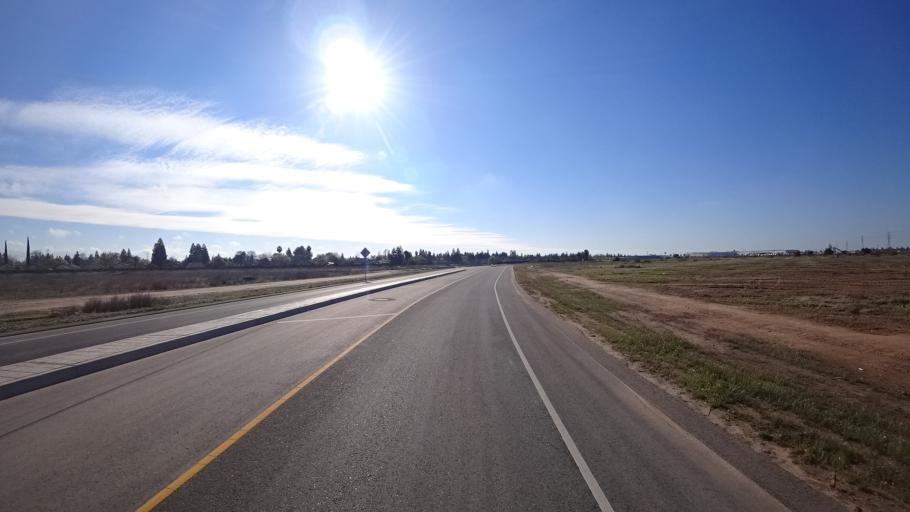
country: US
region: California
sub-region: Fresno County
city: Biola
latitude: 36.8284
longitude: -119.8988
